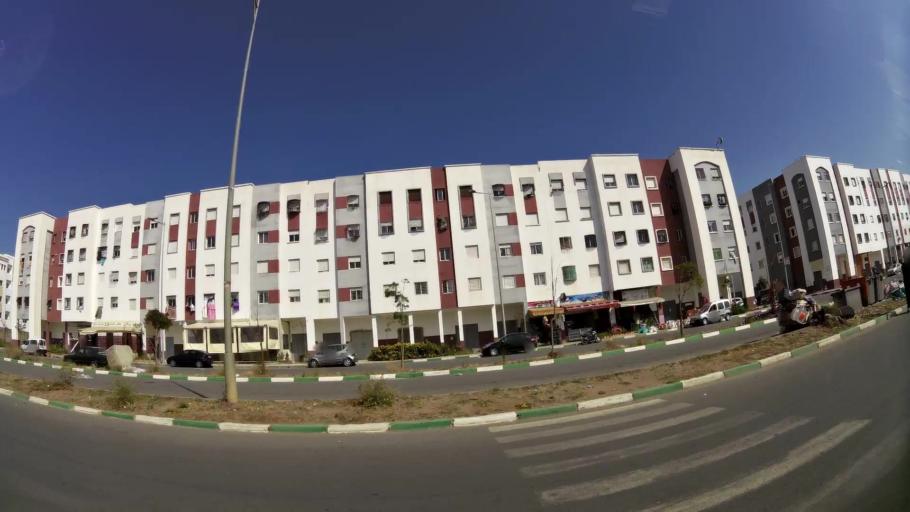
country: MA
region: Rabat-Sale-Zemmour-Zaer
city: Sale
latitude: 34.0659
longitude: -6.7625
